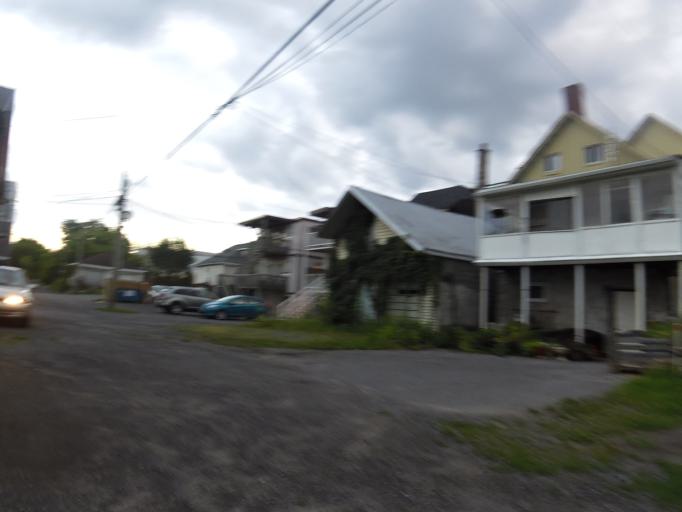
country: CA
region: Ontario
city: Ottawa
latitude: 45.4081
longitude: -75.7296
